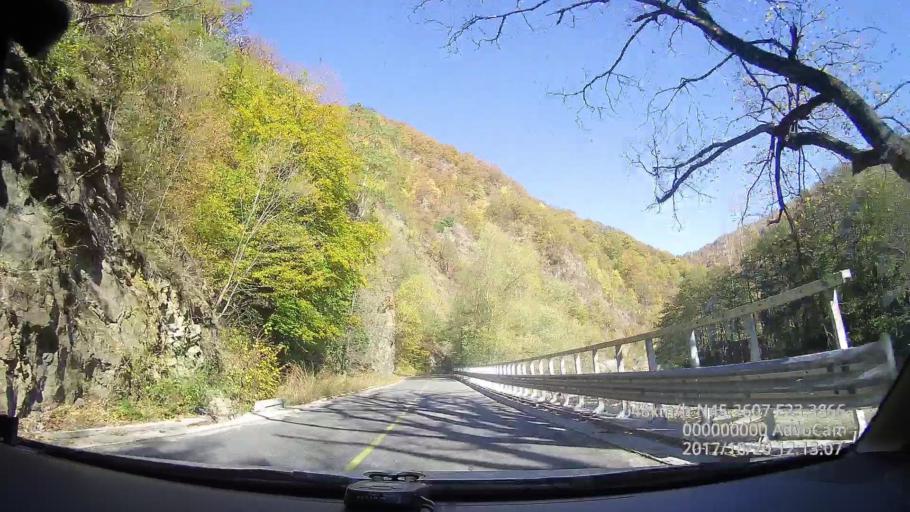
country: RO
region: Gorj
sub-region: Comuna Bumbesti-Jiu
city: Bumbesti-Jiu
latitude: 45.2610
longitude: 23.3865
